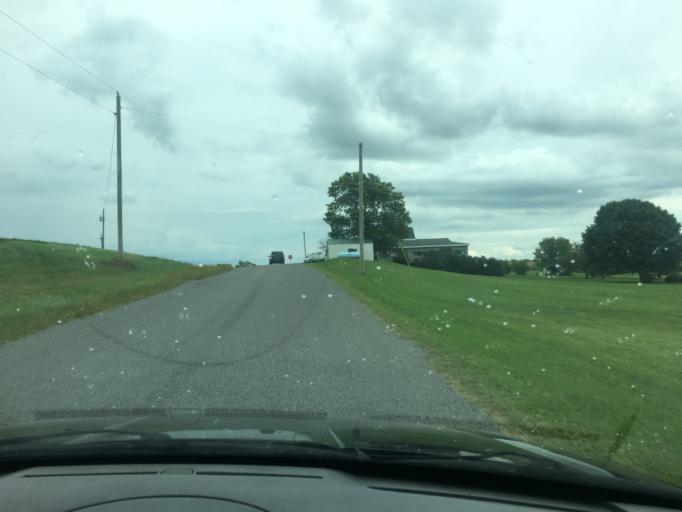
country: US
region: Ohio
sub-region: Logan County
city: West Liberty
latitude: 40.2108
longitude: -83.7029
